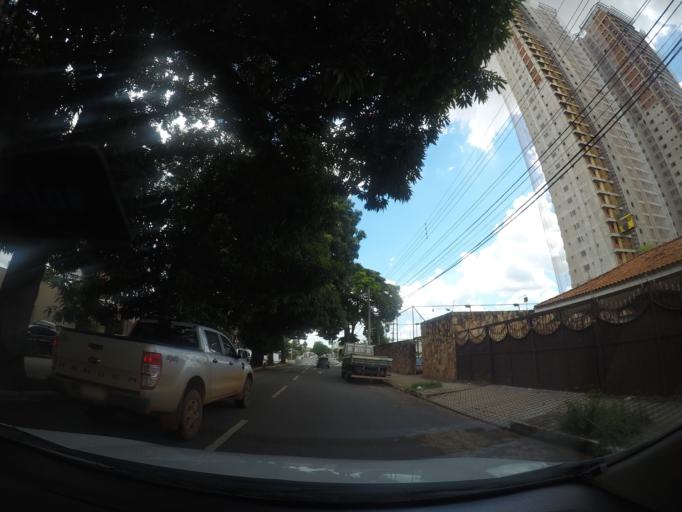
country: BR
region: Goias
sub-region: Goiania
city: Goiania
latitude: -16.6982
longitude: -49.2783
